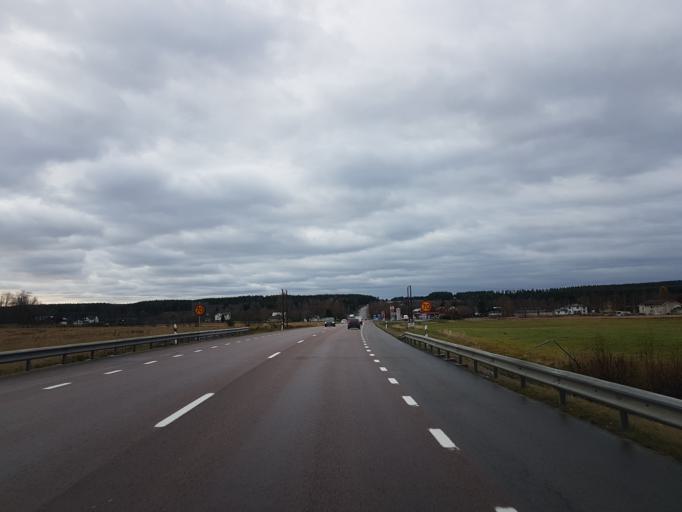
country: SE
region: Gaevleborg
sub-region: Nordanstigs Kommun
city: Bergsjoe
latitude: 62.0487
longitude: 17.2680
